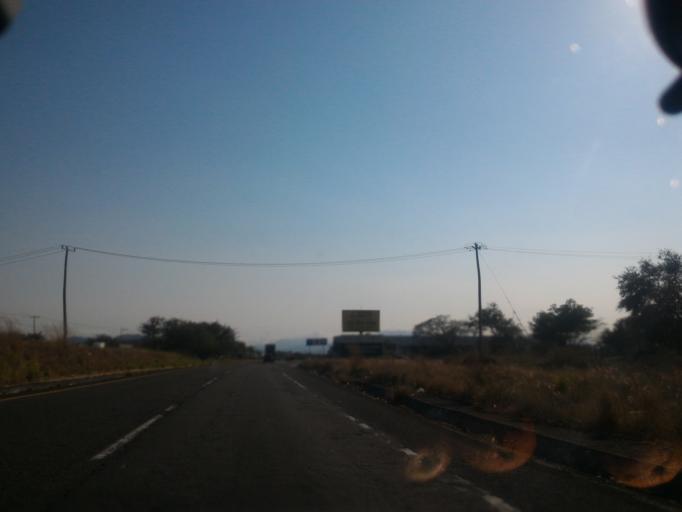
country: MX
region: Colima
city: Colima
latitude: 19.2620
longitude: -103.6827
